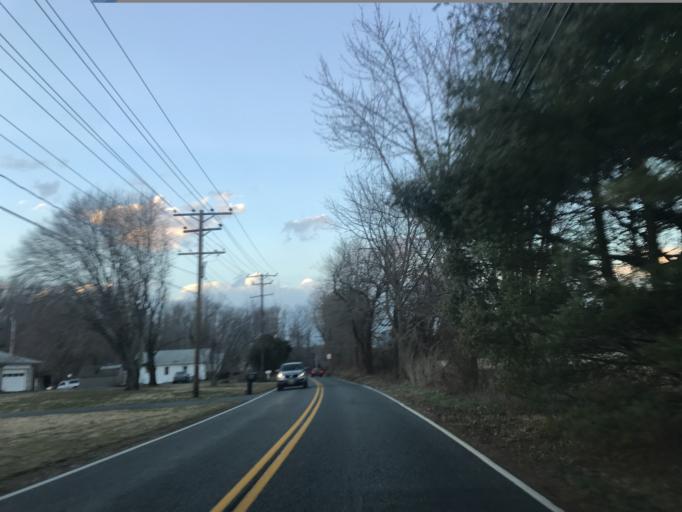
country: US
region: Maryland
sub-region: Harford County
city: Bel Air South
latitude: 39.5443
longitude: -76.2875
